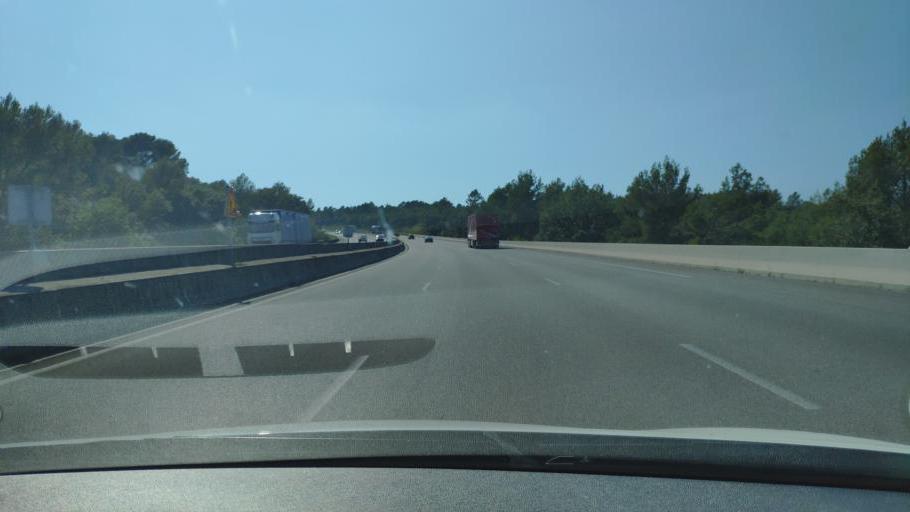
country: FR
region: Provence-Alpes-Cote d'Azur
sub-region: Departement du Var
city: Le Luc
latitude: 43.4052
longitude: 6.2970
